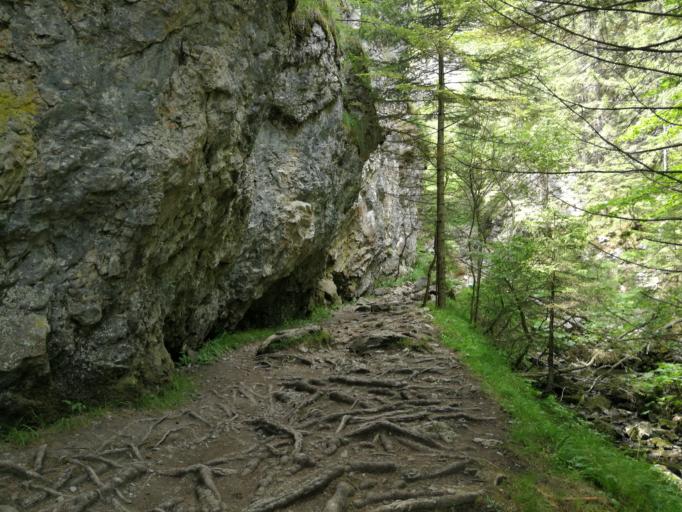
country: SK
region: Zilinsky
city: Tvrdosin
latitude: 49.1973
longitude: 19.5399
